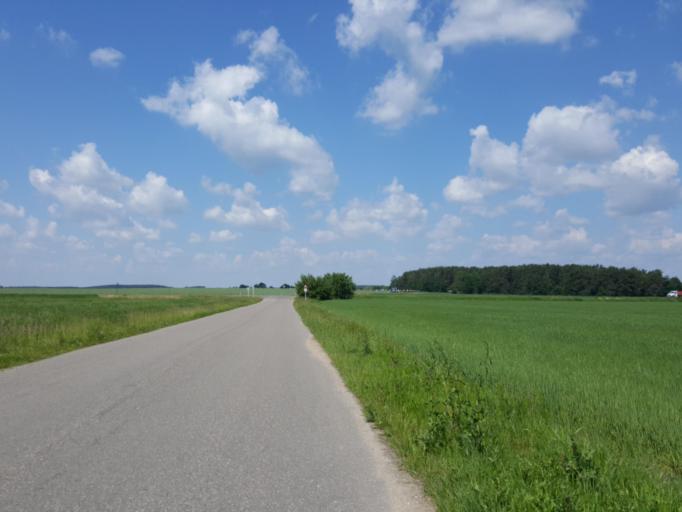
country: BY
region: Brest
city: Kamyanyets
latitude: 52.3813
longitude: 23.7906
